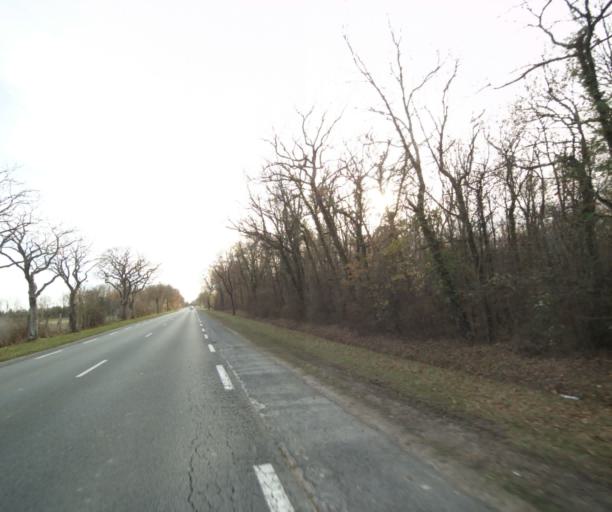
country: FR
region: Poitou-Charentes
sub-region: Departement de la Charente-Maritime
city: Fontcouverte
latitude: 45.7839
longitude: -0.5705
